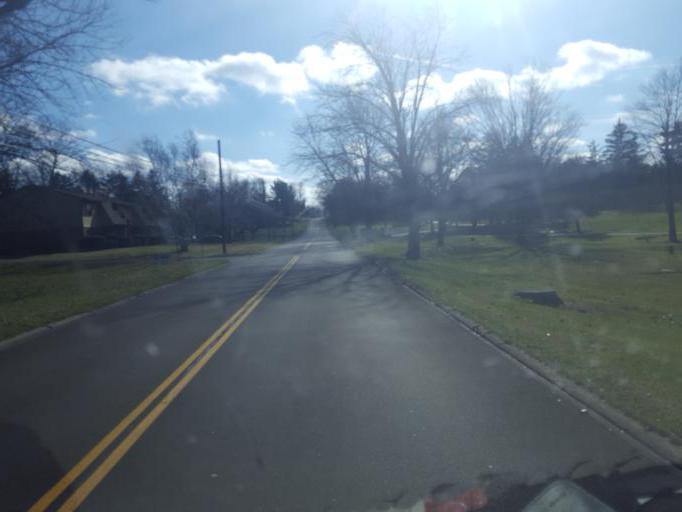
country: US
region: Ohio
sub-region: Richland County
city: Ontario
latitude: 40.7580
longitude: -82.6030
